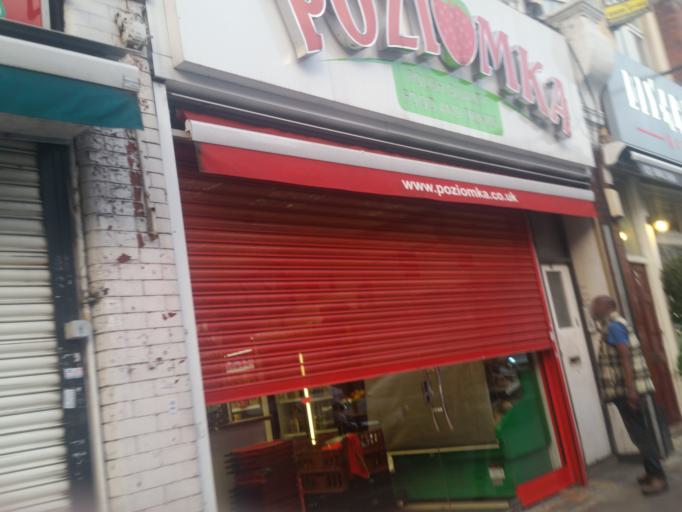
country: GB
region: England
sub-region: Greater London
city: Harringay
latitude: 51.5791
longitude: -0.0990
